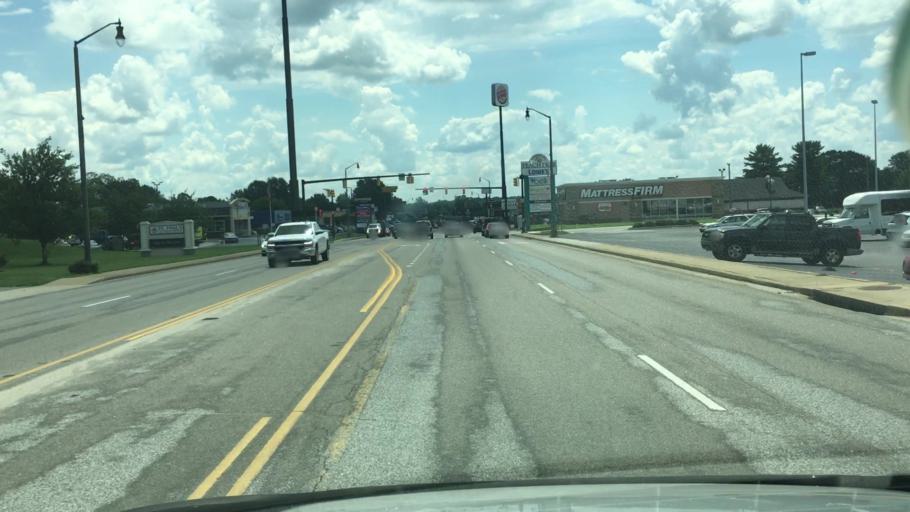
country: US
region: South Carolina
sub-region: Cherokee County
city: Gaffney
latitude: 35.0929
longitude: -81.6647
